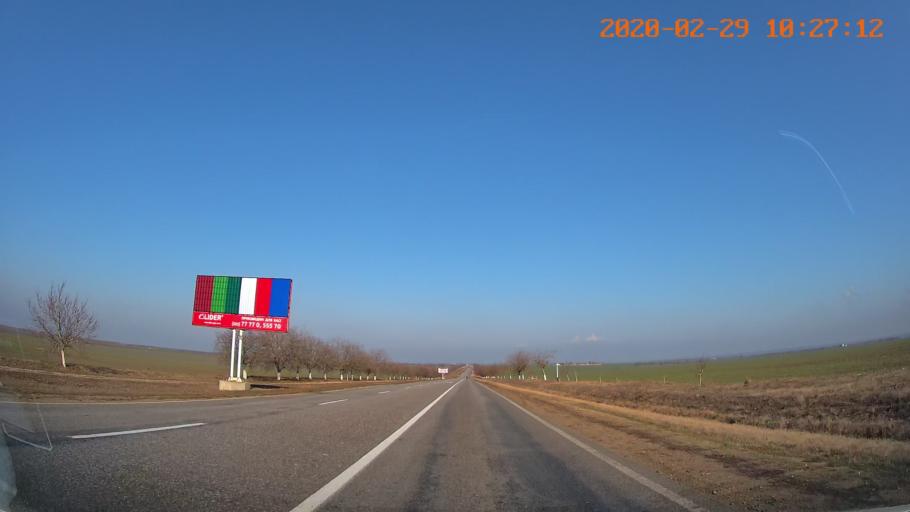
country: MD
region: Telenesti
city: Tiraspolul Nou
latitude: 46.8927
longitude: 29.5993
